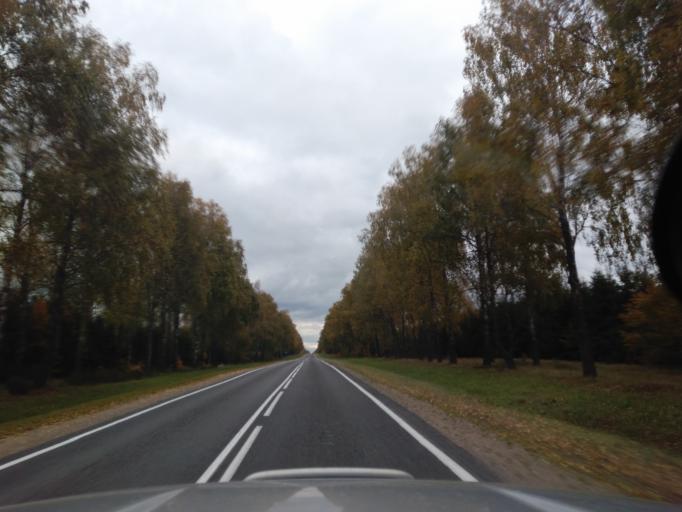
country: BY
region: Minsk
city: Slutsk
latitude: 53.2218
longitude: 27.4977
